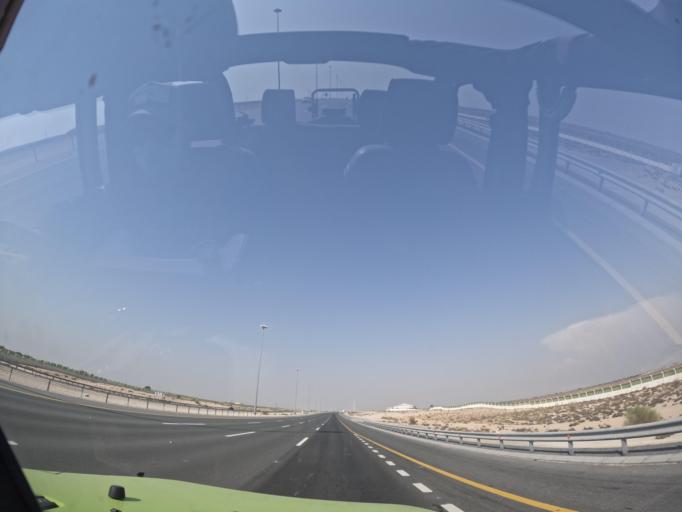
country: AE
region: Abu Dhabi
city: Abu Dhabi
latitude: 24.6258
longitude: 54.7728
